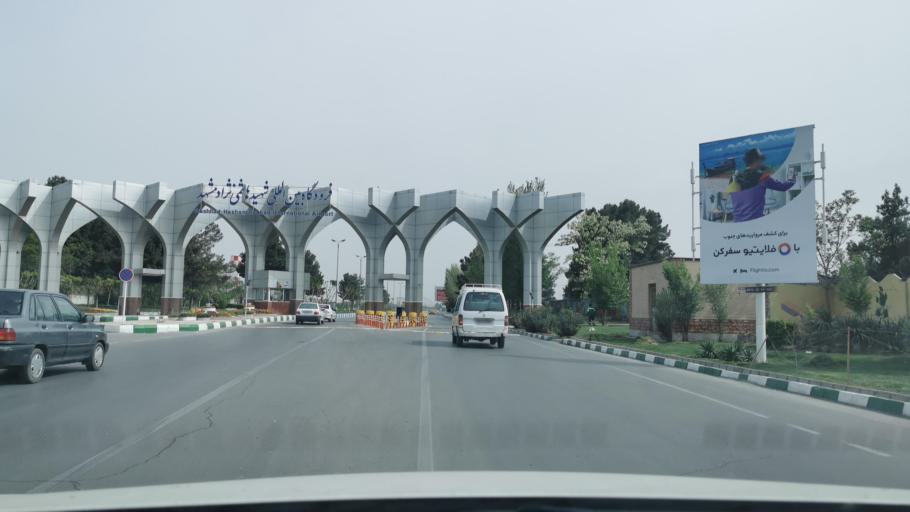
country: IR
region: Razavi Khorasan
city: Mashhad
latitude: 36.2420
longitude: 59.6245
